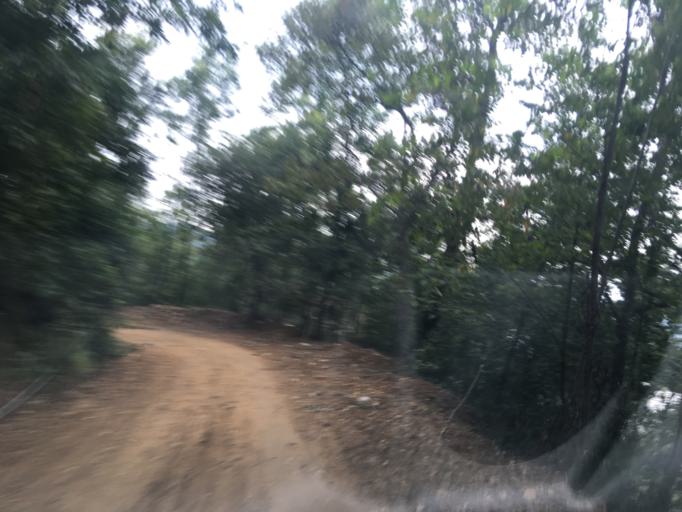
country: CN
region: Guangxi Zhuangzu Zizhiqu
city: Xinzhou
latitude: 25.1679
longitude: 105.6852
